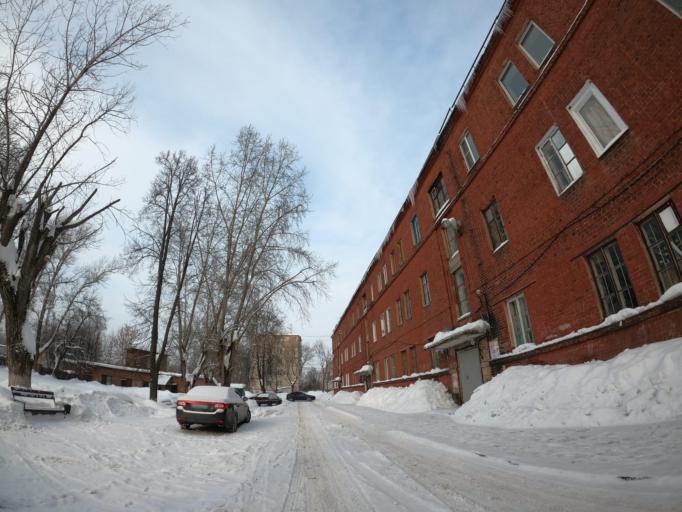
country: RU
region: Moskovskaya
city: Elektrogorsk
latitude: 55.8893
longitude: 38.7719
